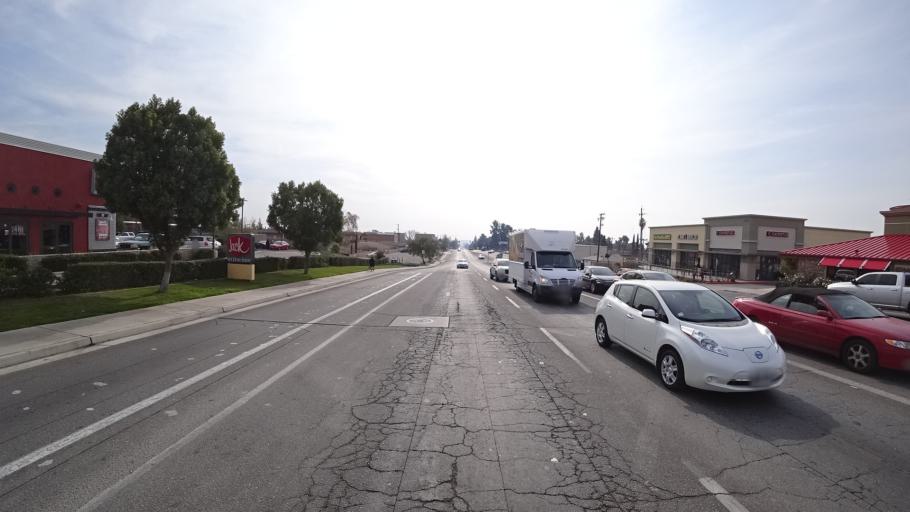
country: US
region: California
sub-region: Kern County
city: Bakersfield
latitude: 35.3927
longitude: -118.9674
